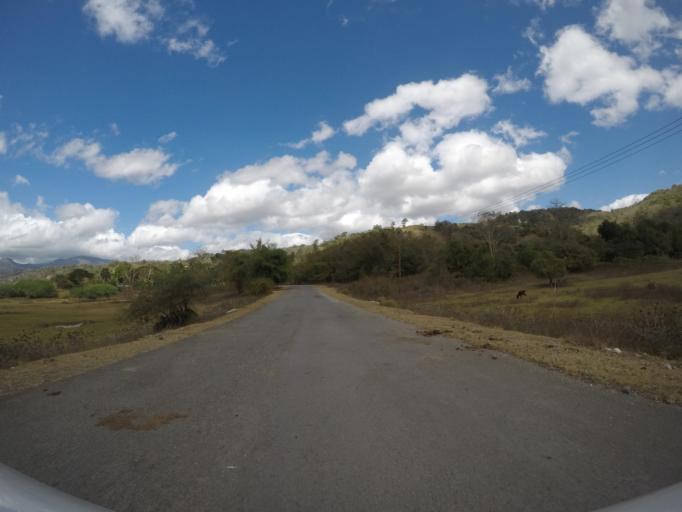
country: TL
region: Lautem
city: Lospalos
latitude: -8.4683
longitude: 126.8184
